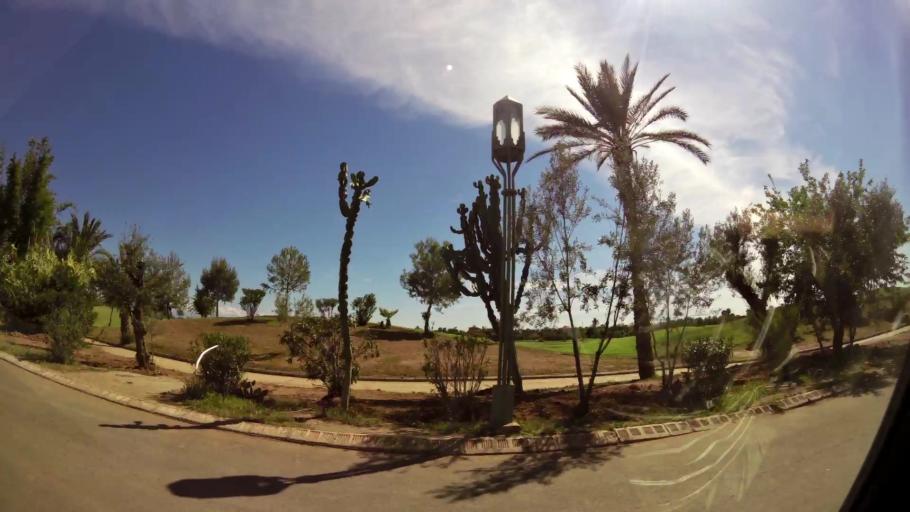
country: MA
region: Marrakech-Tensift-Al Haouz
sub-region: Marrakech
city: Marrakesh
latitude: 31.6190
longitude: -7.9374
